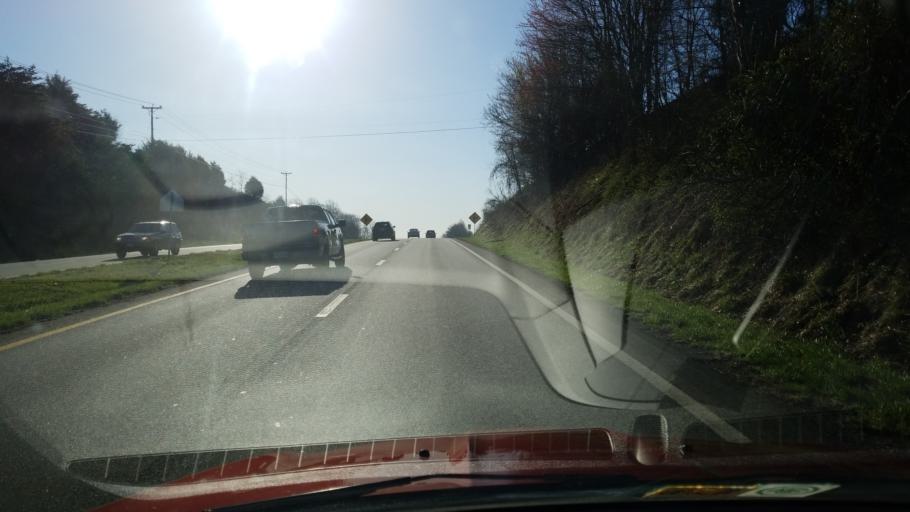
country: US
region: Virginia
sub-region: Franklin County
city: Rocky Mount
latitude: 37.0853
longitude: -79.9289
